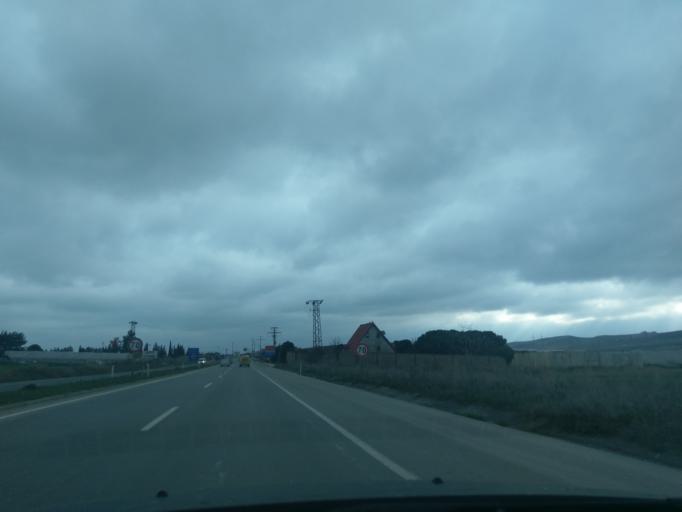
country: TR
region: Istanbul
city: Muratbey
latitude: 41.1012
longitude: 28.5088
